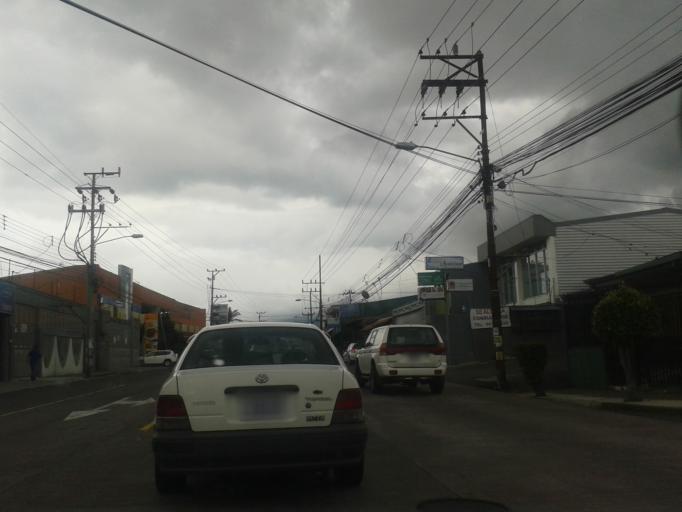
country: CR
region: San Jose
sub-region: Canton de Goicoechea
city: Guadalupe
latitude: 9.9508
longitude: -84.0578
